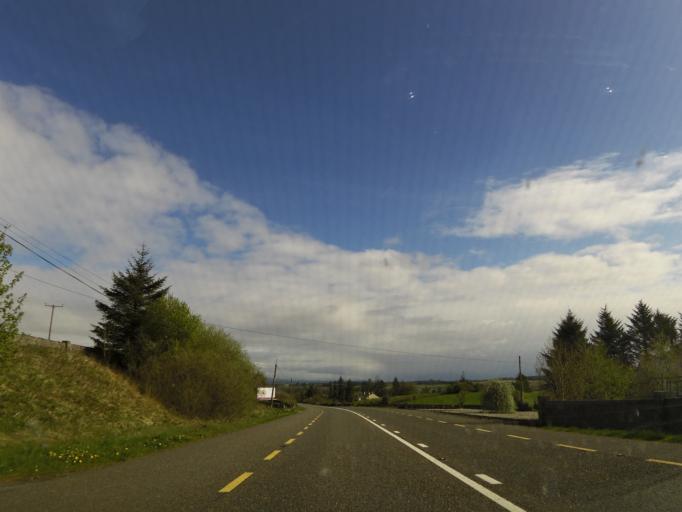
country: IE
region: Connaught
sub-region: Sligo
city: Tobercurry
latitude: 53.9206
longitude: -8.7866
